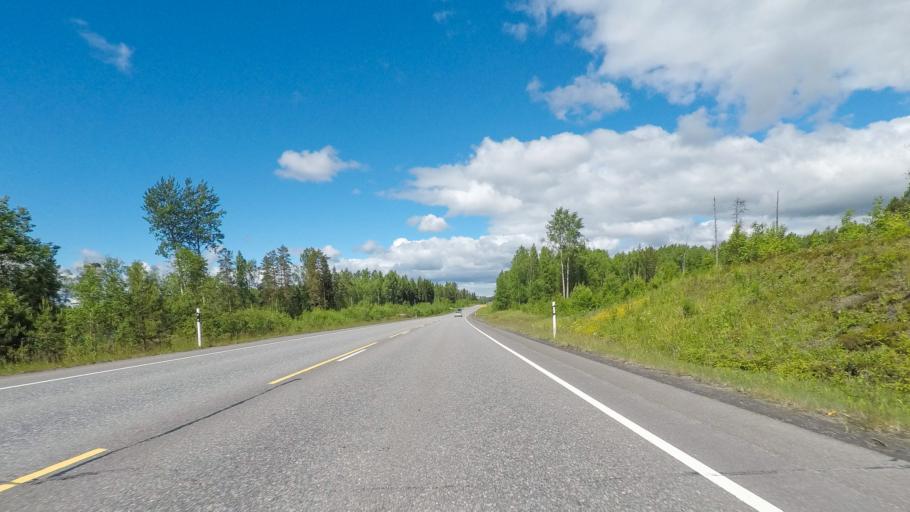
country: FI
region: Paijanne Tavastia
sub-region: Lahti
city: Heinola
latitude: 61.3323
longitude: 26.0403
